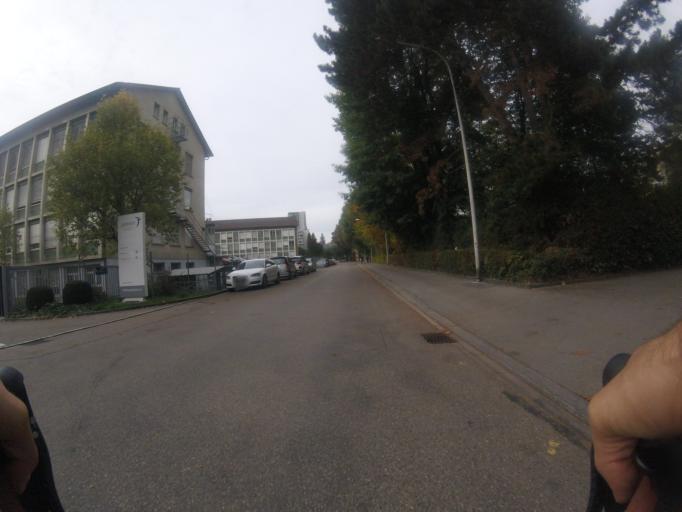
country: CH
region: Bern
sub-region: Bern-Mittelland District
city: Koniz
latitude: 46.9350
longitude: 7.3874
